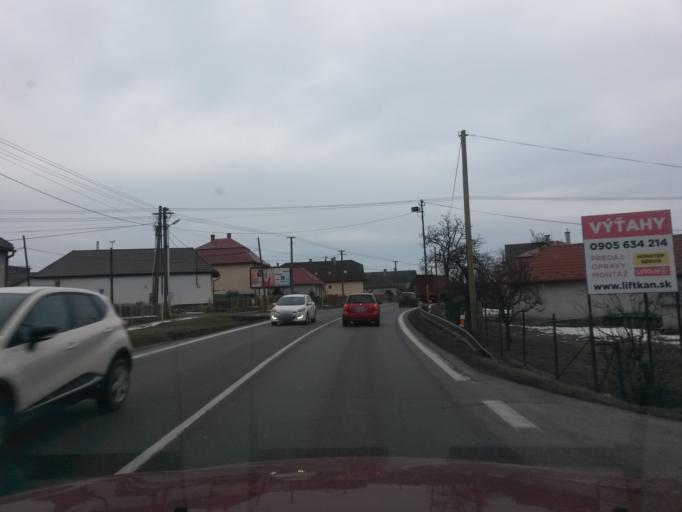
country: SK
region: Kosicky
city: Secovce
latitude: 48.7332
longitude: 21.5809
